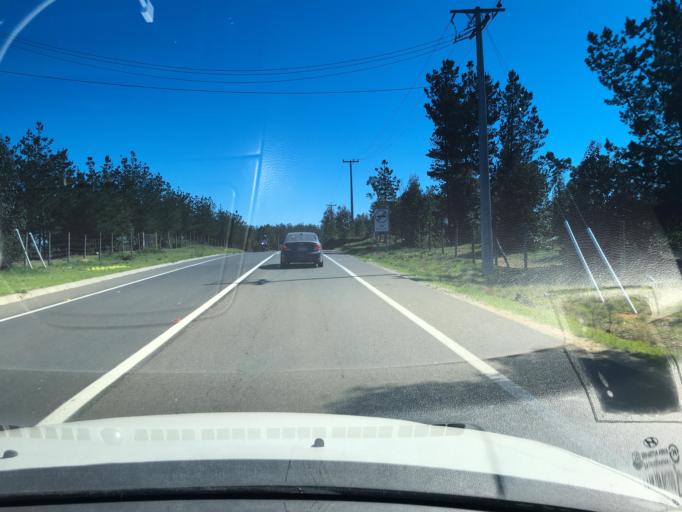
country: CL
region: Valparaiso
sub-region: San Antonio Province
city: El Tabo
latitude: -33.4227
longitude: -71.6762
